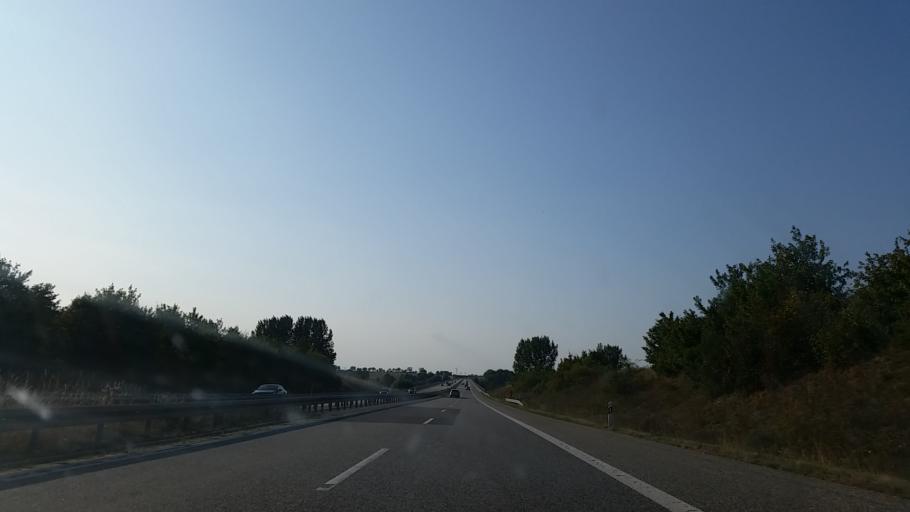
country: DE
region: Mecklenburg-Vorpommern
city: Pasewalk
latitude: 53.4756
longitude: 13.9501
